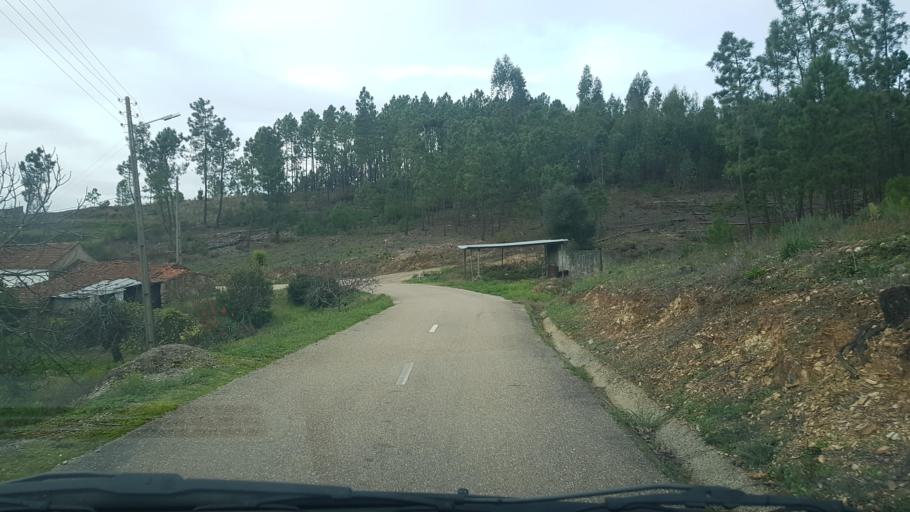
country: PT
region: Castelo Branco
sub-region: Vila de Rei
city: Vila de Rei
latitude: 39.6012
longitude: -8.1228
